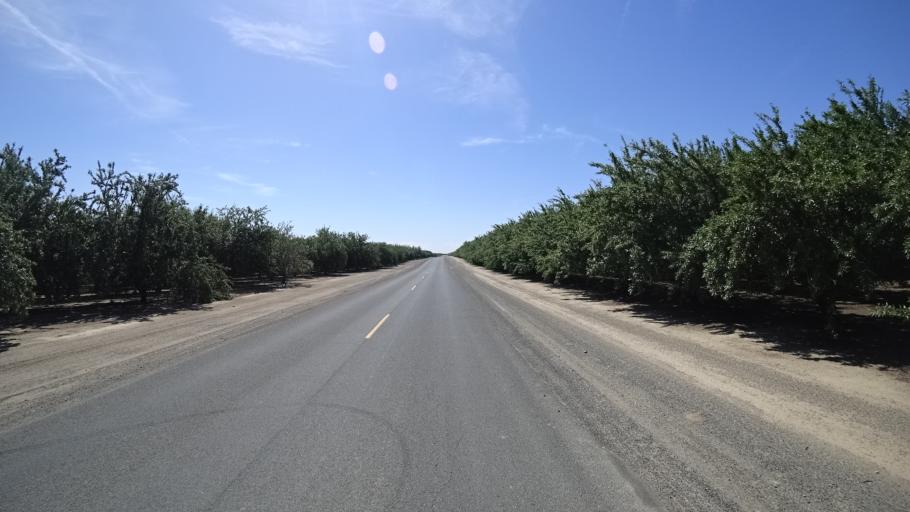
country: US
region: California
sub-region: Kings County
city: Kettleman City
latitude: 35.9773
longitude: -119.9473
